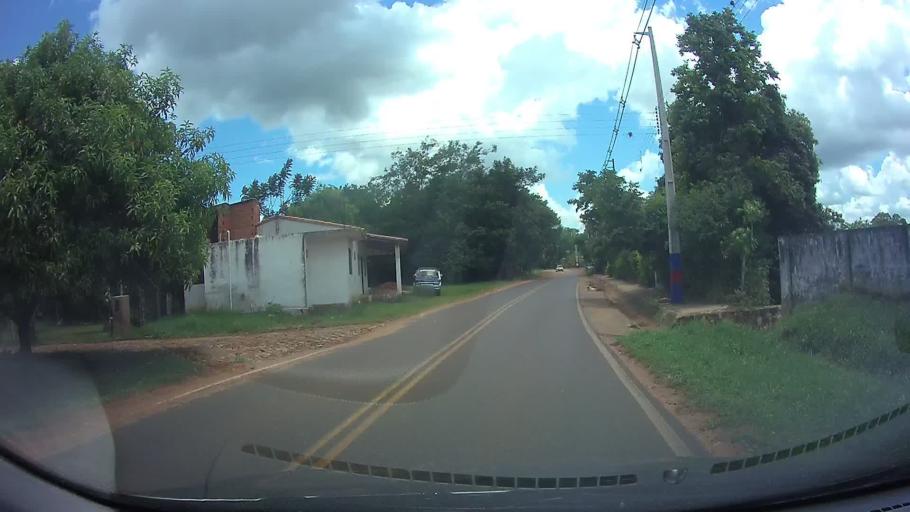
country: PY
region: Central
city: Capiata
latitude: -25.3297
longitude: -57.4224
